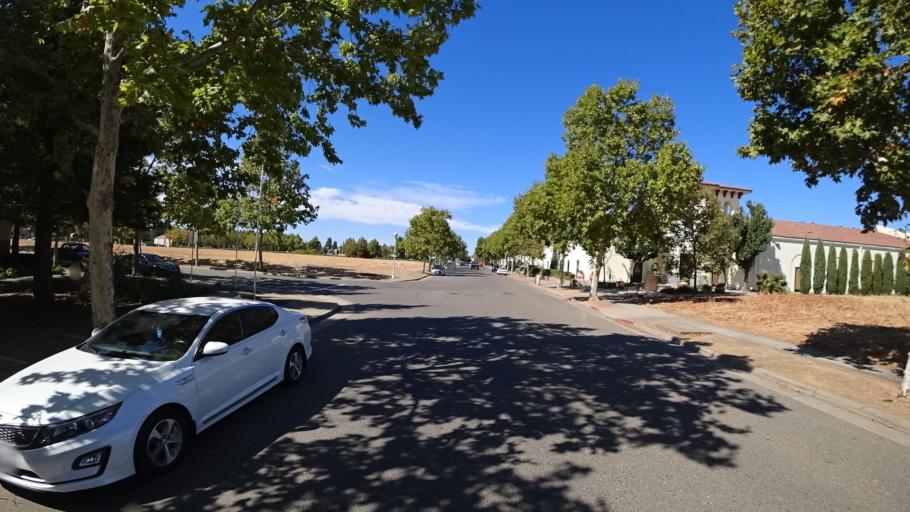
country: US
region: California
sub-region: Sacramento County
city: Laguna
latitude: 38.4264
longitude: -121.4685
